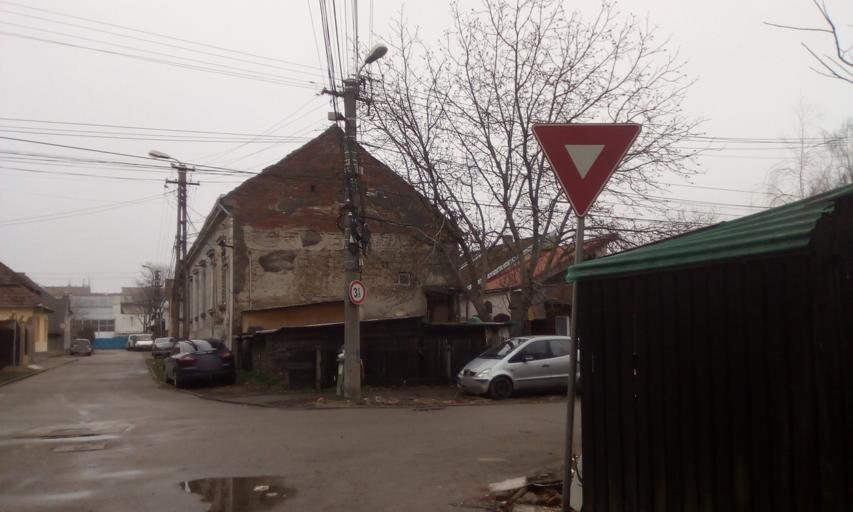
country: RO
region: Timis
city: Timisoara
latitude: 45.7500
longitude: 21.2477
